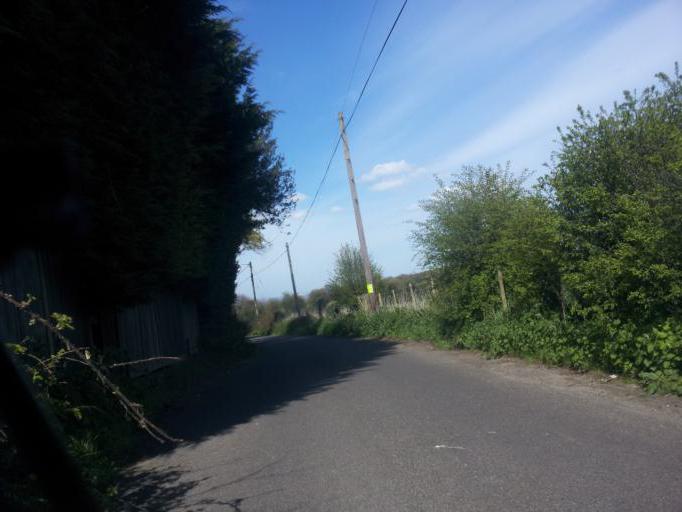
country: GB
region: England
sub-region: Kent
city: Rainham
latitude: 51.3162
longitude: 0.6134
